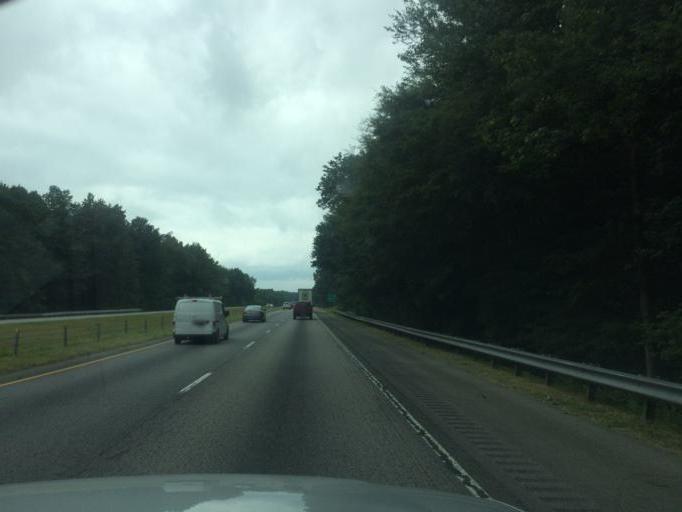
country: US
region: Georgia
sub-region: Banks County
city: Homer
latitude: 34.3090
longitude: -83.3859
